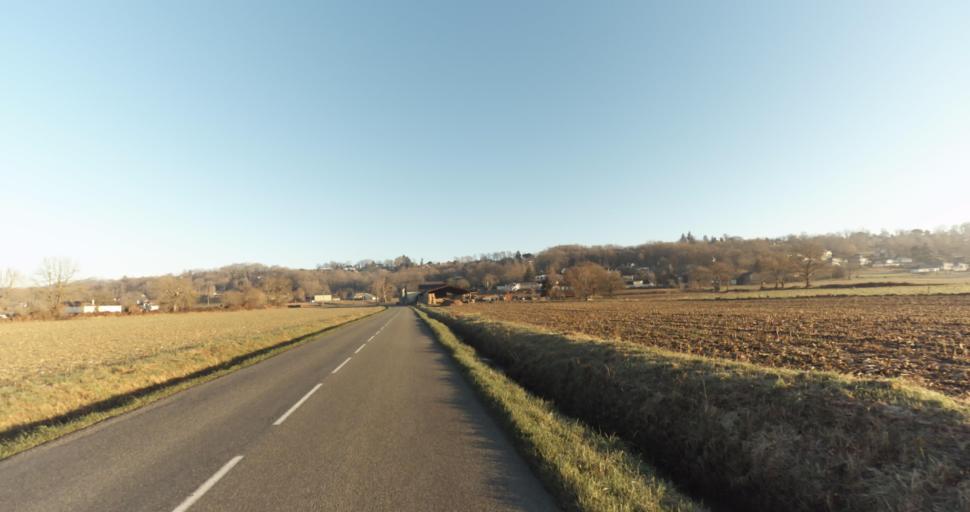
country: FR
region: Aquitaine
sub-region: Departement des Pyrenees-Atlantiques
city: Morlaas
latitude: 43.3230
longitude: -0.2738
